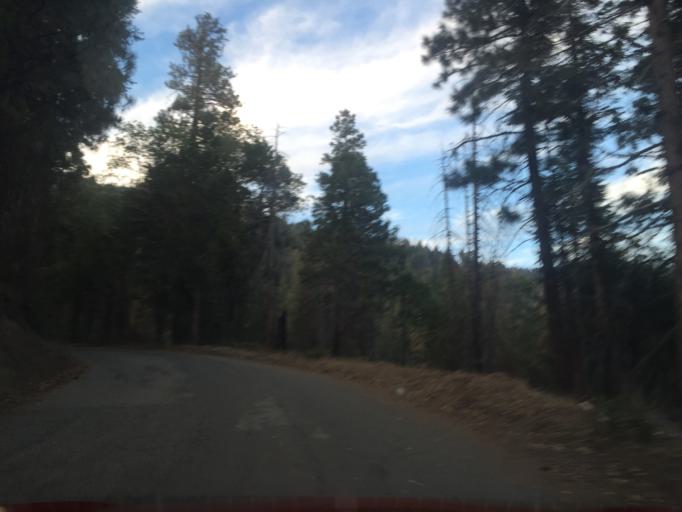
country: US
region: California
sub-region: Tulare County
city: Three Rivers
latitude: 36.4524
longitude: -118.6890
